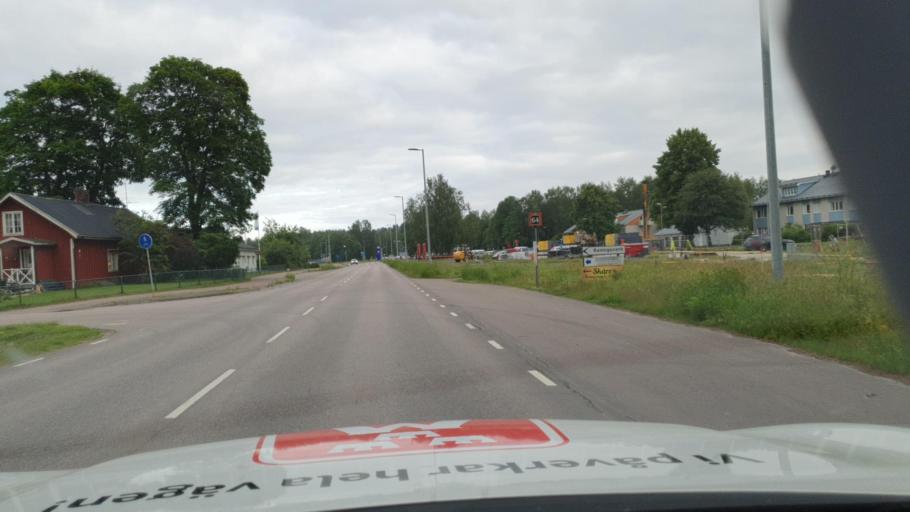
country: SE
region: Vaermland
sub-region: Karlstads Kommun
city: Karlstad
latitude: 59.4368
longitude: 13.4427
